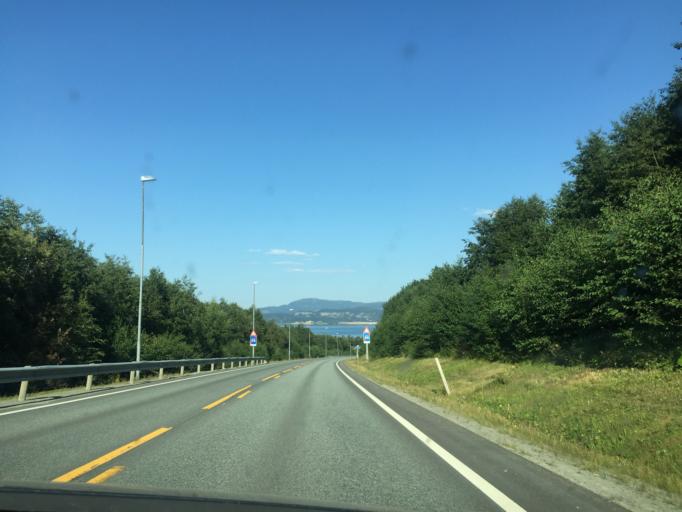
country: NO
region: Sor-Trondelag
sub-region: Malvik
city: Malvik
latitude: 63.4278
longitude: 10.6959
